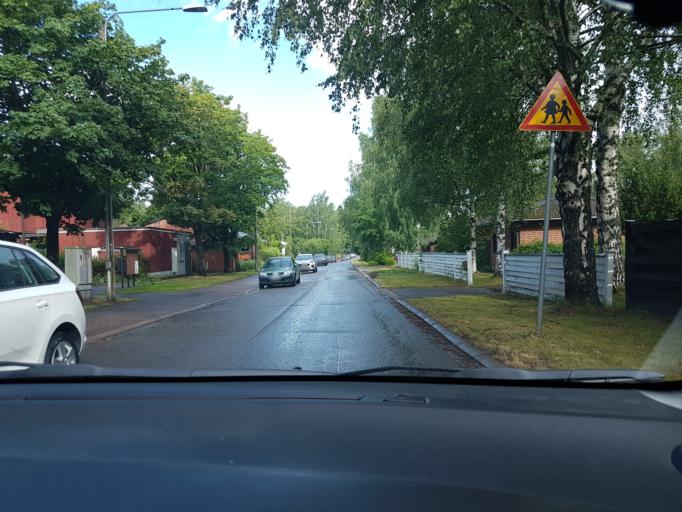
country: FI
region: Uusimaa
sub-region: Helsinki
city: Vantaa
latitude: 60.2385
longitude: 25.0181
